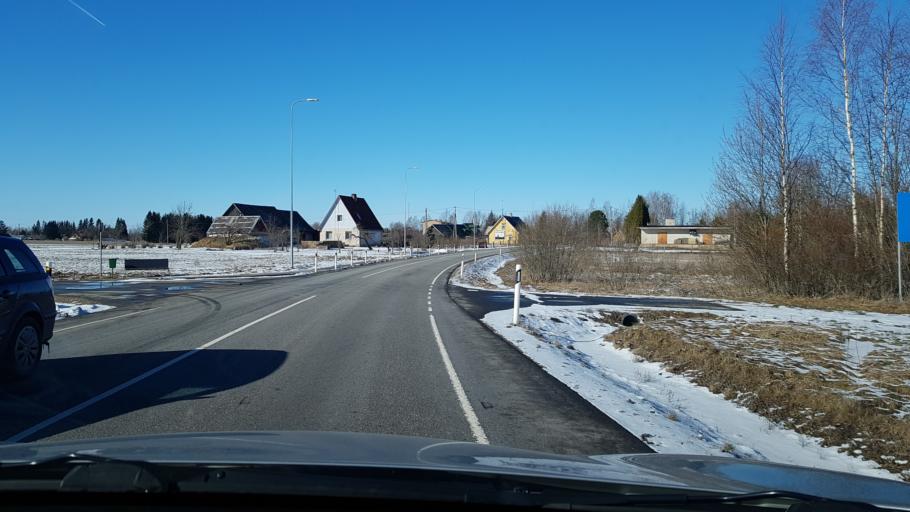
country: EE
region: Polvamaa
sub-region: Raepina vald
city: Rapina
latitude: 57.9990
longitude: 27.5460
